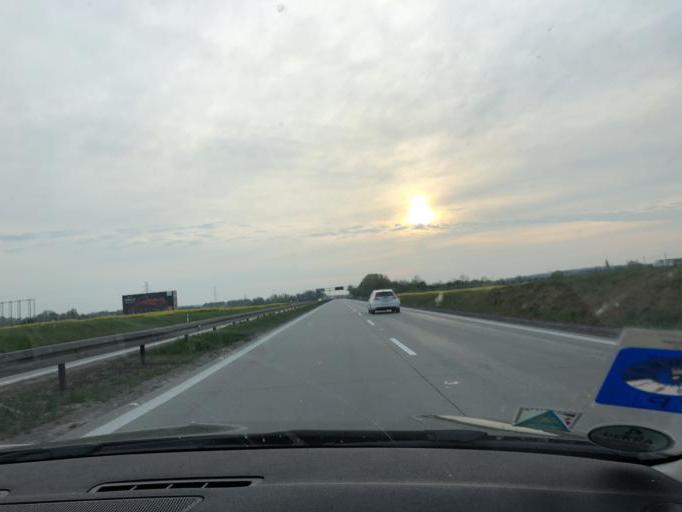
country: PL
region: Lower Silesian Voivodeship
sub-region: Legnica
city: Legnica
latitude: 51.1615
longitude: 16.1570
